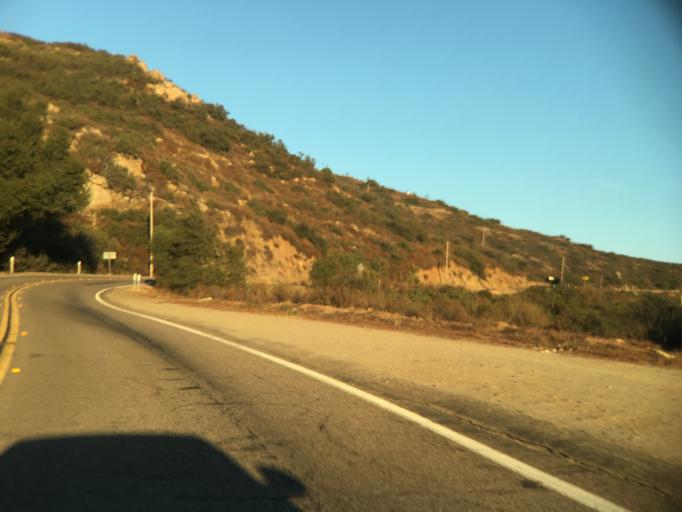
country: US
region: California
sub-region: San Diego County
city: Alpine
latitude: 32.8051
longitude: -116.7871
